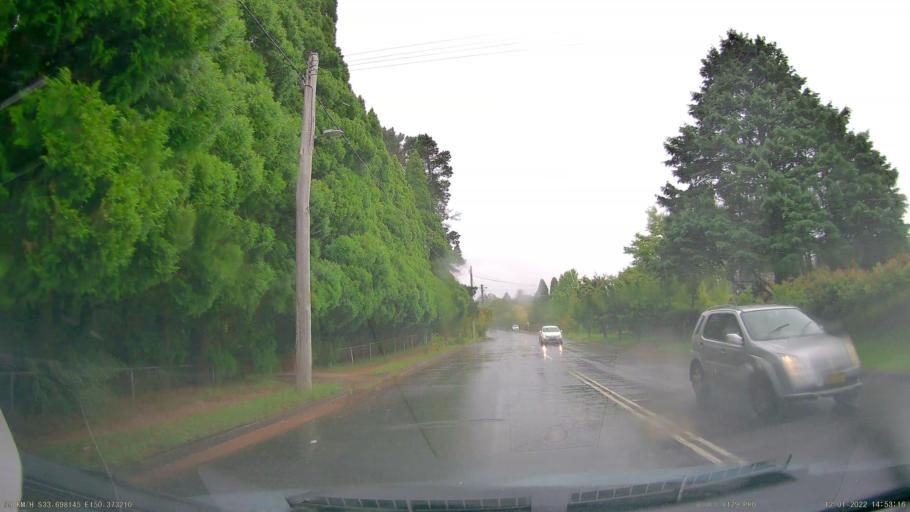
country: AU
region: New South Wales
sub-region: Blue Mountains Municipality
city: Leura
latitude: -33.6982
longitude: 150.3732
